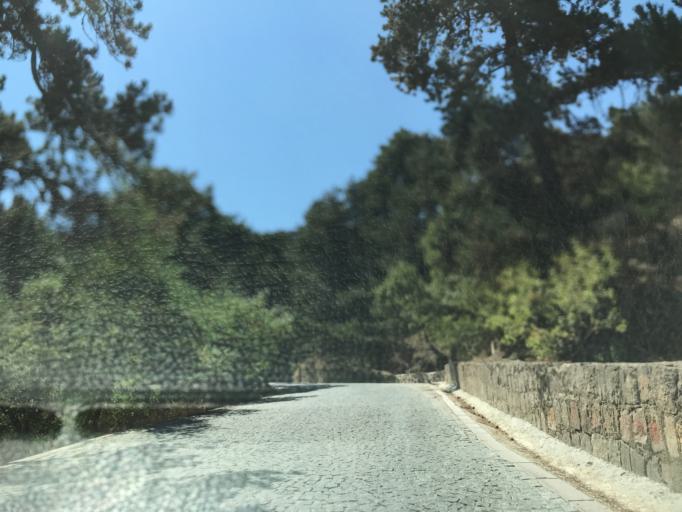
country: TR
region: Yozgat
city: Yozgat
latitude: 39.8055
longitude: 34.8092
